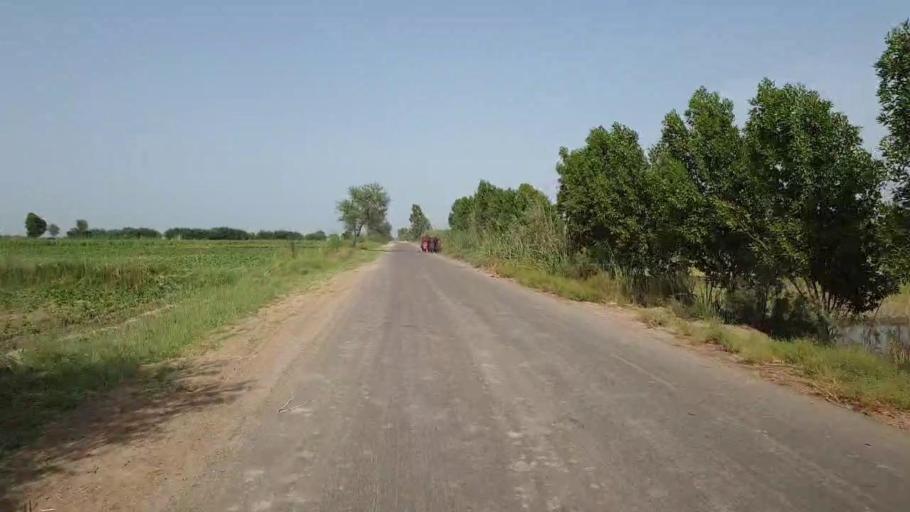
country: PK
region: Sindh
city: Sakrand
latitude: 26.2844
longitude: 68.2492
